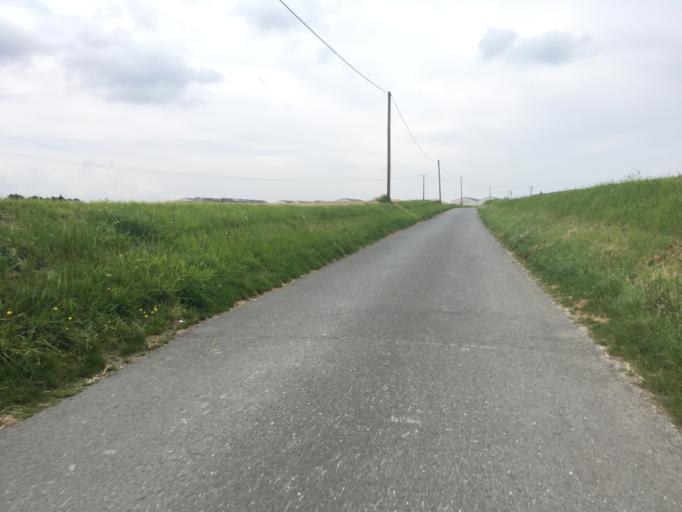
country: FR
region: Poitou-Charentes
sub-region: Departement de la Charente-Maritime
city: Aytre
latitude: 46.1449
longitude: -1.1216
